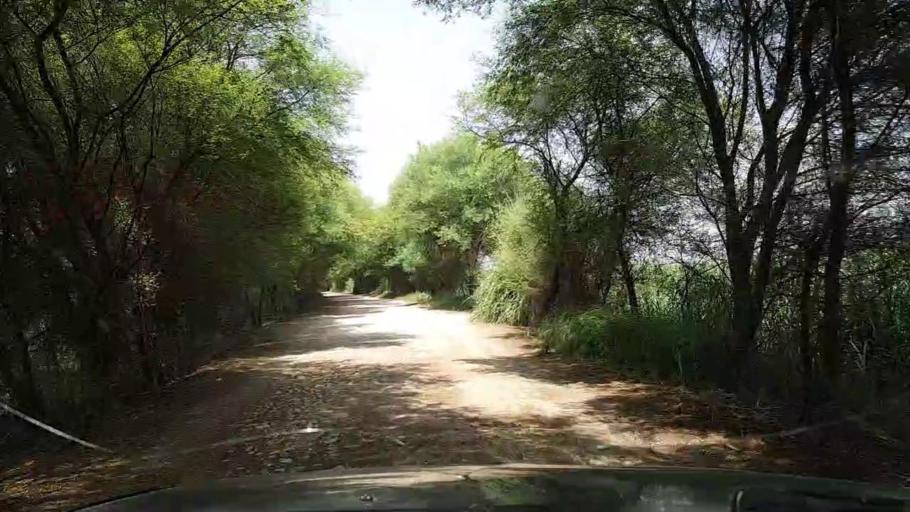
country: PK
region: Sindh
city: Ghotki
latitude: 28.0916
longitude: 69.3123
